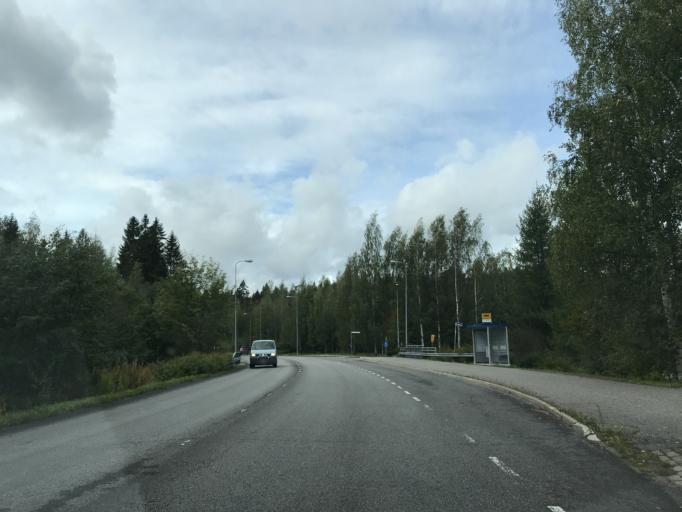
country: FI
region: Paijanne Tavastia
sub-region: Lahti
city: Lahti
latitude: 61.0020
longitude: 25.7607
